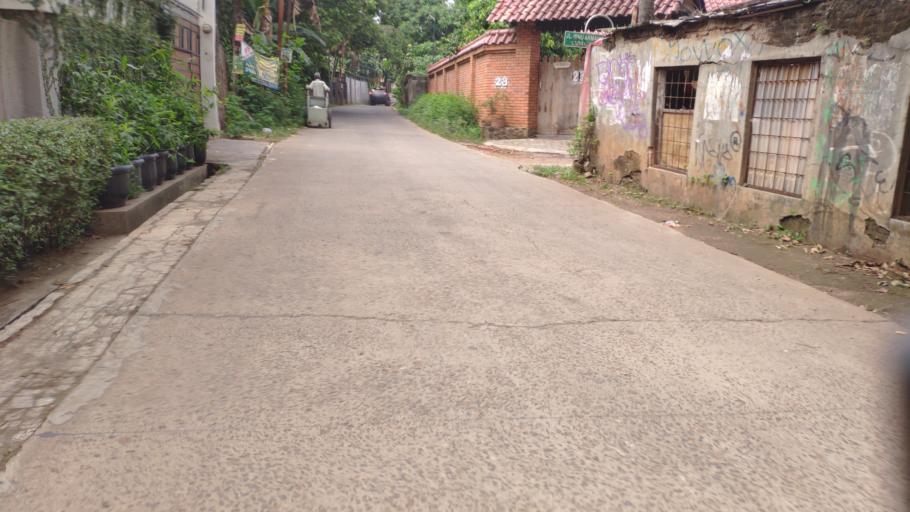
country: ID
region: West Java
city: Pamulang
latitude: -6.3277
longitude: 106.8000
